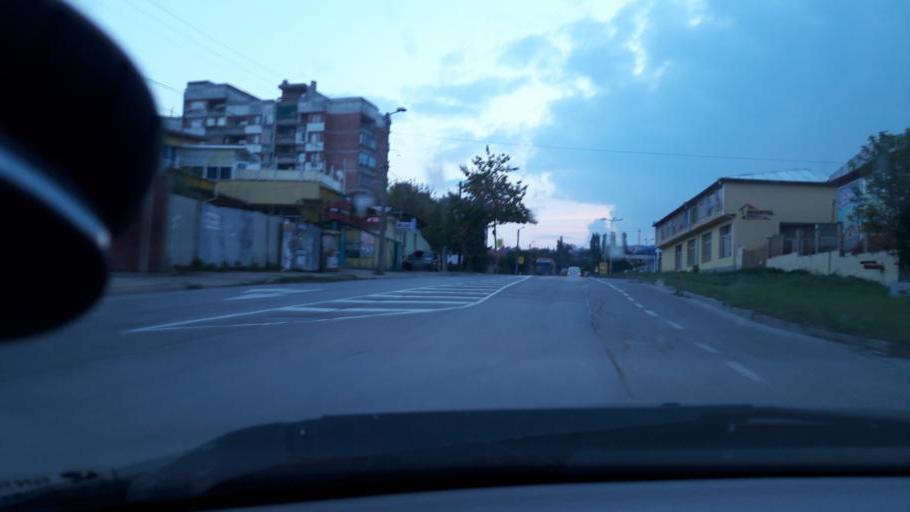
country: BG
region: Razgrad
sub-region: Obshtina Razgrad
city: Razgrad
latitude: 43.5307
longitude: 26.5137
